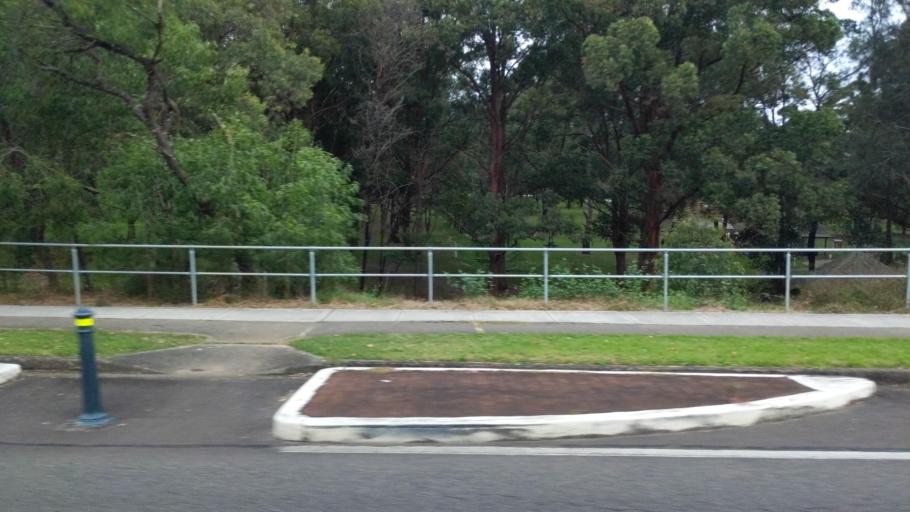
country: AU
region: New South Wales
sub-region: The Hills Shire
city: Baulkham Hills
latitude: -33.7475
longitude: 150.9683
